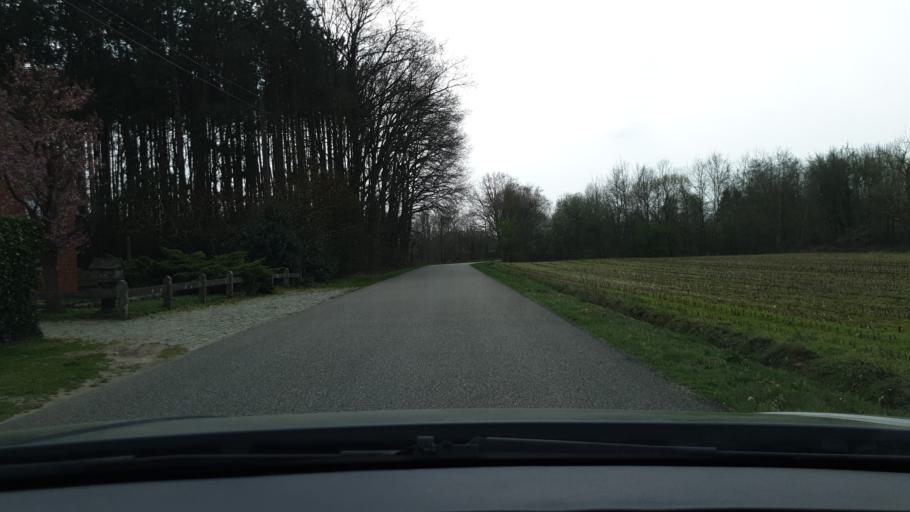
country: BE
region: Flanders
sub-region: Provincie Antwerpen
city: Geel
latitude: 51.1313
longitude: 4.9985
